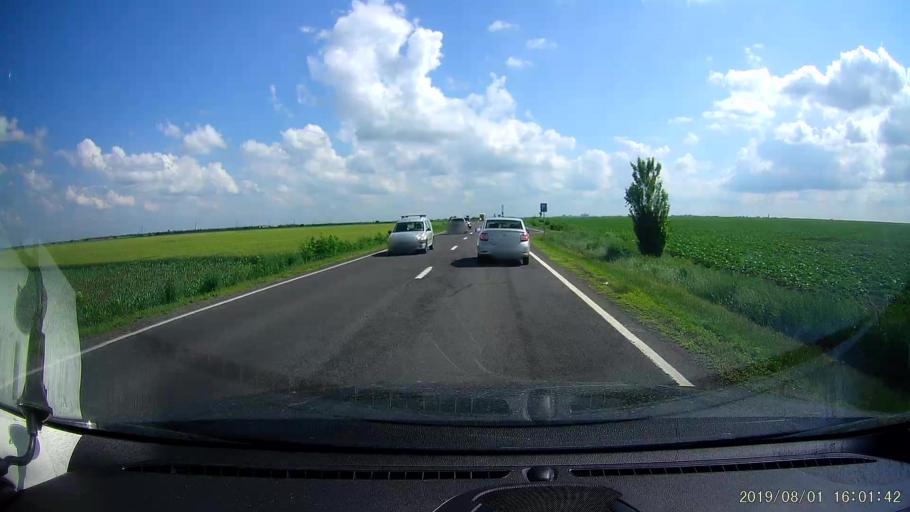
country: RO
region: Ialomita
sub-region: Comuna Ciulnita
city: Ciulnita
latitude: 44.5035
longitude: 27.3896
